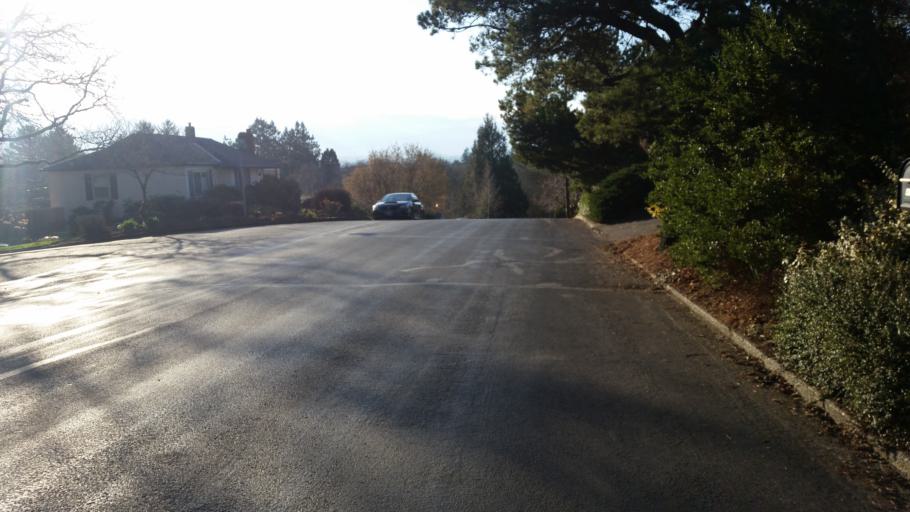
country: US
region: Oregon
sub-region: Washington County
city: Raleigh Hills
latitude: 45.4813
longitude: -122.7240
